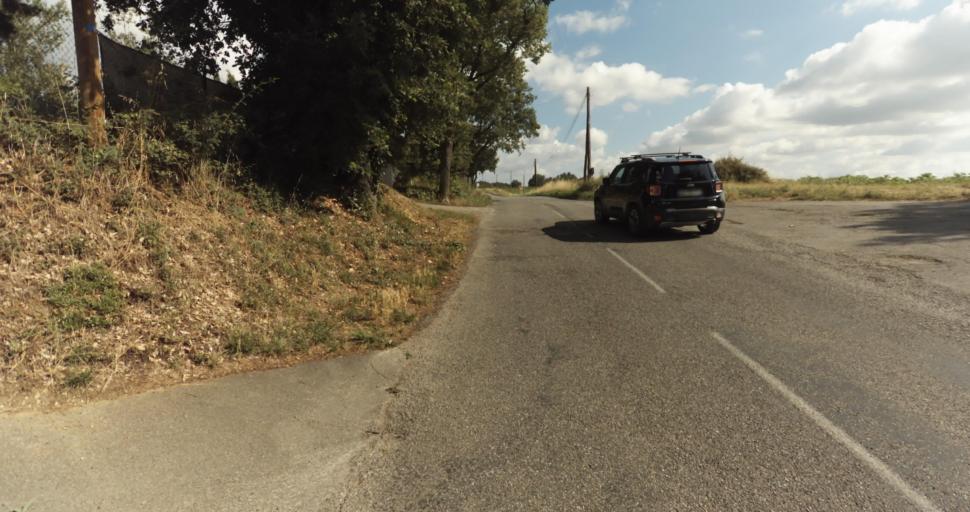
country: FR
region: Midi-Pyrenees
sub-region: Departement de la Haute-Garonne
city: Fonsorbes
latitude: 43.5673
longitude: 1.2334
